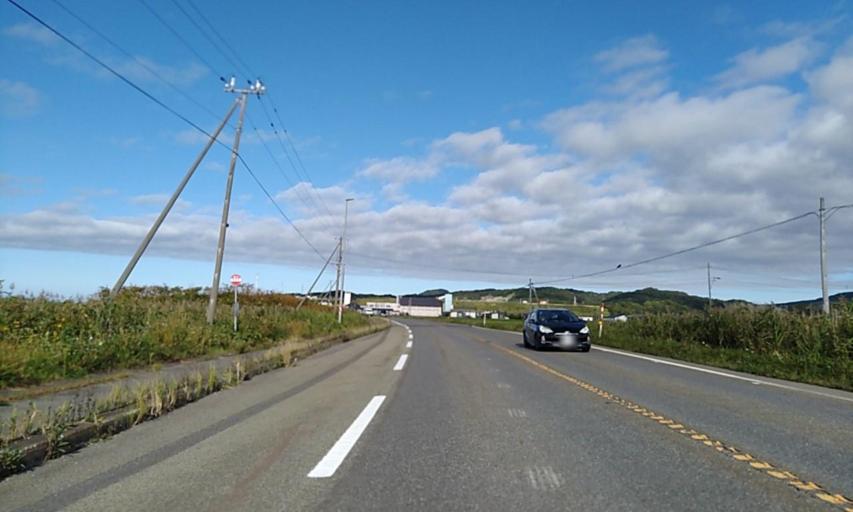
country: JP
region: Hokkaido
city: Shizunai-furukawacho
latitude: 42.2437
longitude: 142.5860
